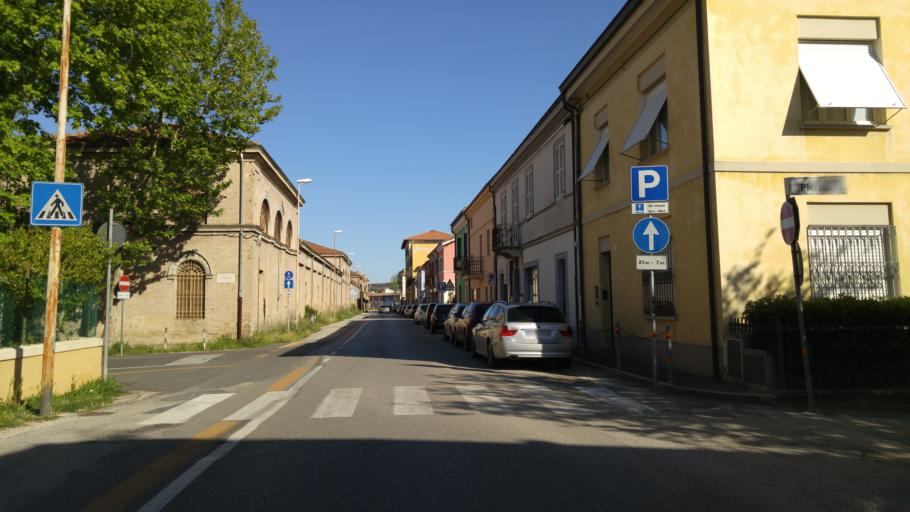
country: IT
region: The Marches
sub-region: Provincia di Pesaro e Urbino
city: Fano
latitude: 43.8405
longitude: 13.0143
